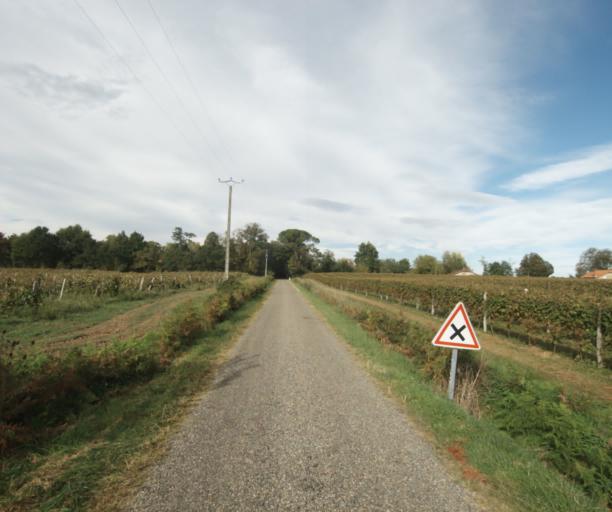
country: FR
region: Midi-Pyrenees
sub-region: Departement du Gers
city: Le Houga
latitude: 43.8785
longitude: -0.1681
